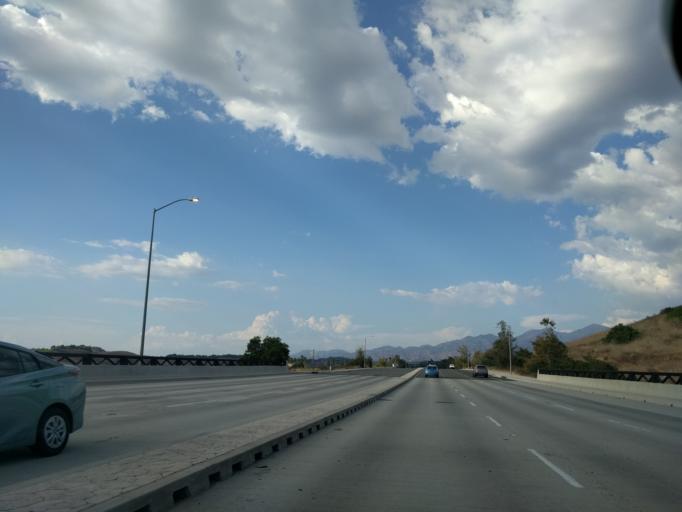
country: US
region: California
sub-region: Orange County
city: Ladera Ranch
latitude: 33.5765
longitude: -117.6327
